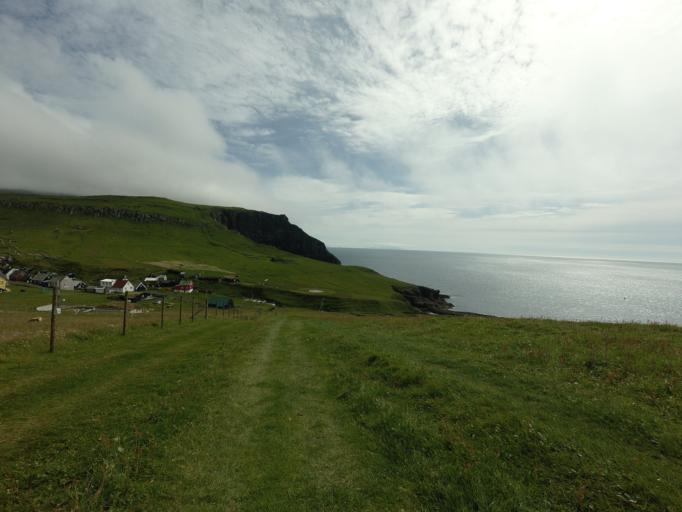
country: FO
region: Vagar
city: Sorvagur
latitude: 62.1035
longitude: -7.6491
